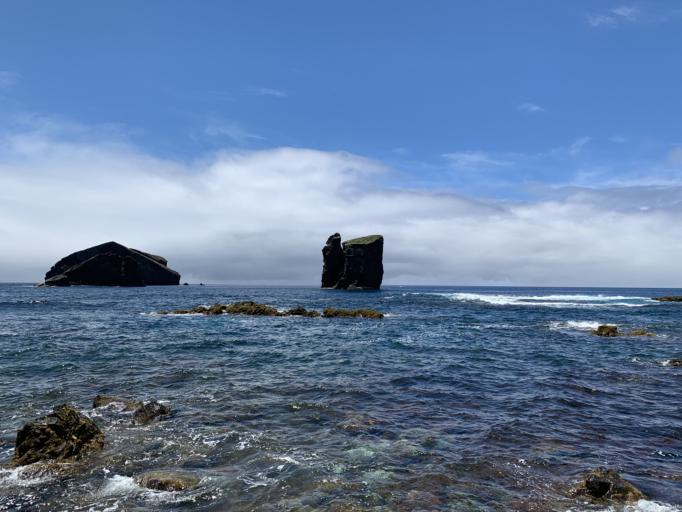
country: PT
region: Azores
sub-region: Ponta Delgada
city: Arrifes
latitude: 37.8899
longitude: -25.8255
